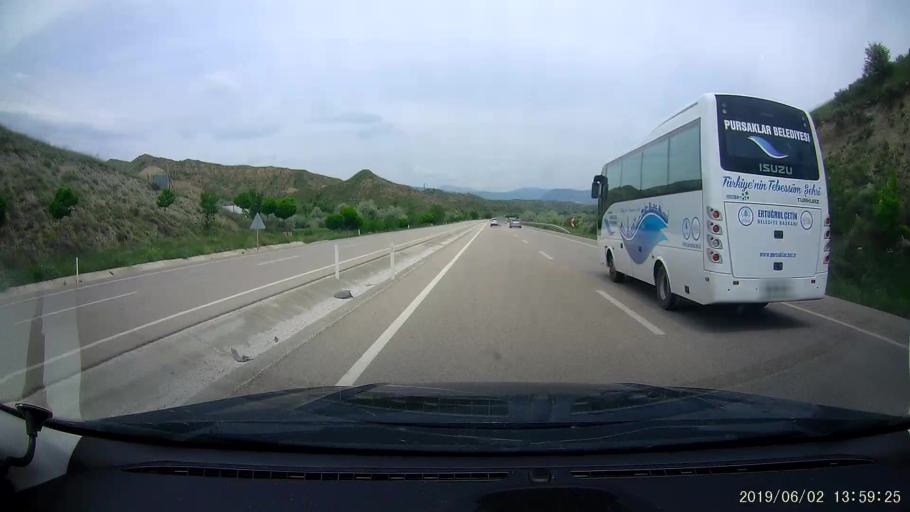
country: TR
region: Cankiri
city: Beloren
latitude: 40.8940
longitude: 33.5424
